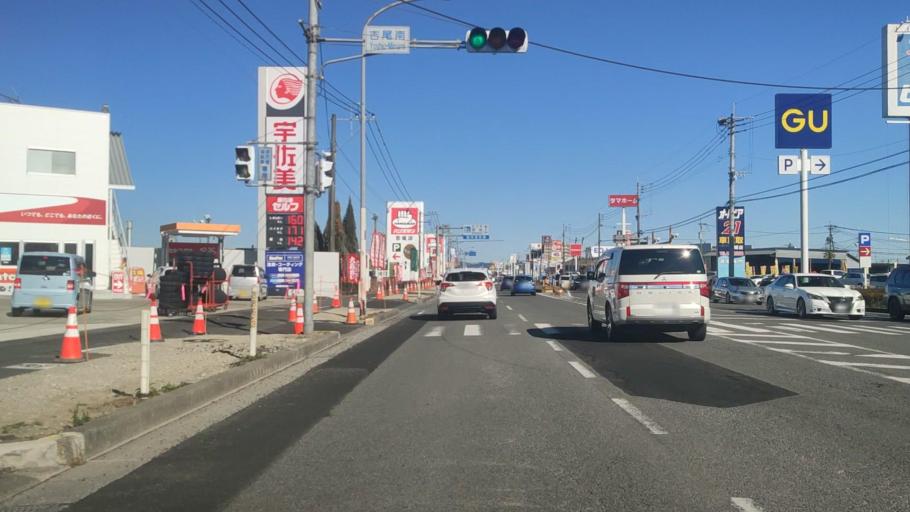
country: JP
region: Miyazaki
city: Miyakonojo
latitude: 31.7537
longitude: 131.0802
